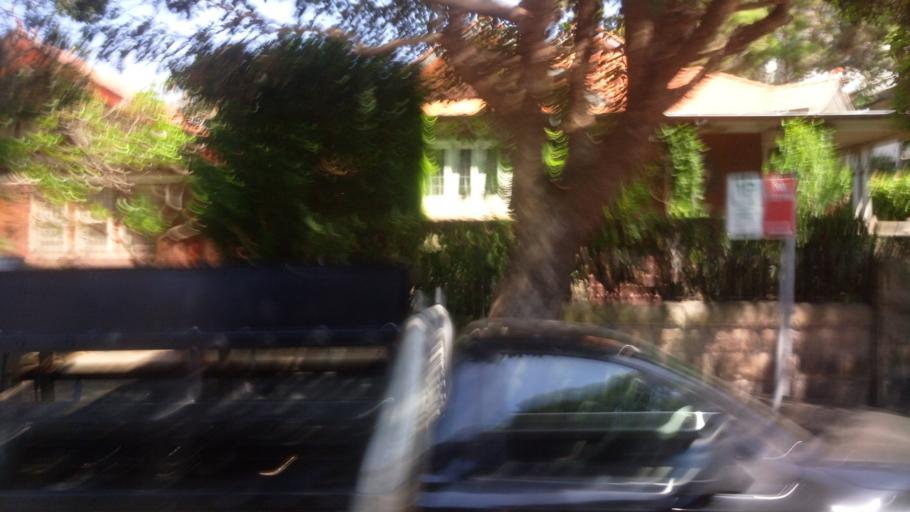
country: AU
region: New South Wales
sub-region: Randwick
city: Kingsford
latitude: -33.9192
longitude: 151.2359
